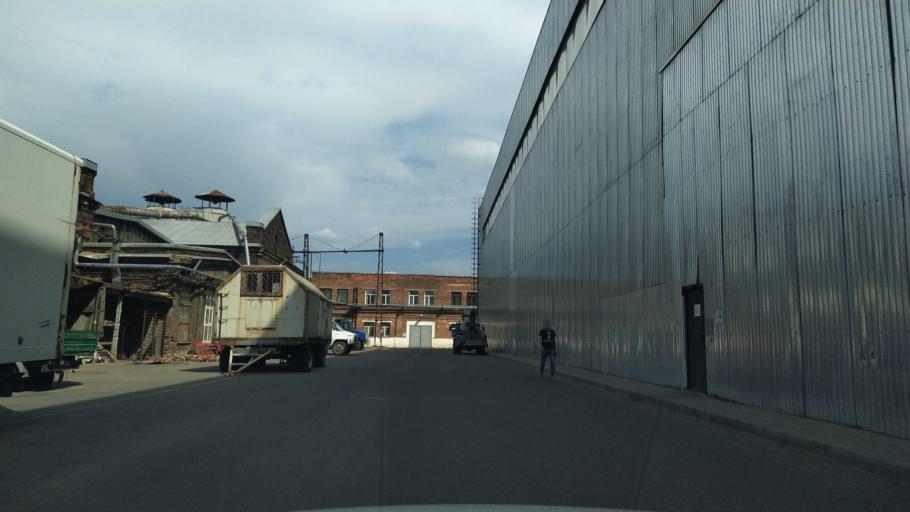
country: RU
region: Leningrad
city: Finlyandskiy
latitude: 59.9608
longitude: 30.3642
